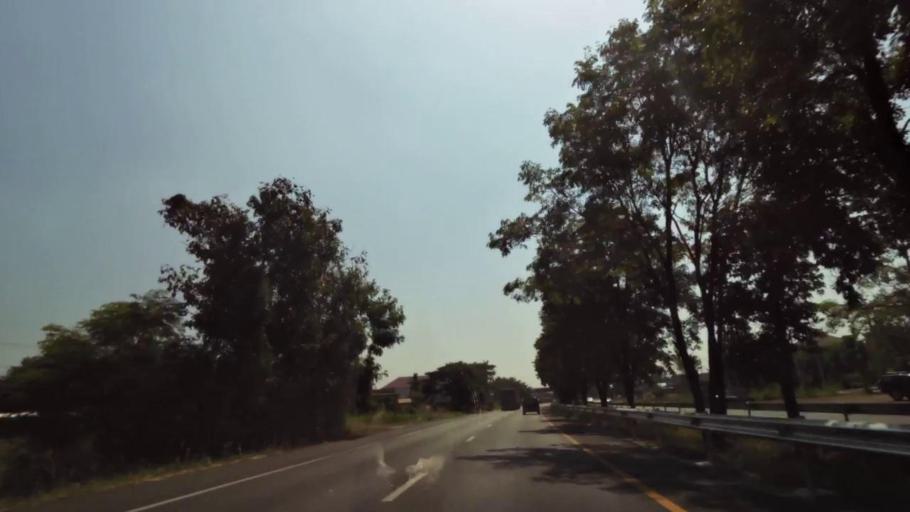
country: TH
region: Nakhon Sawan
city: Kao Liao
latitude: 15.9637
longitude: 100.1197
